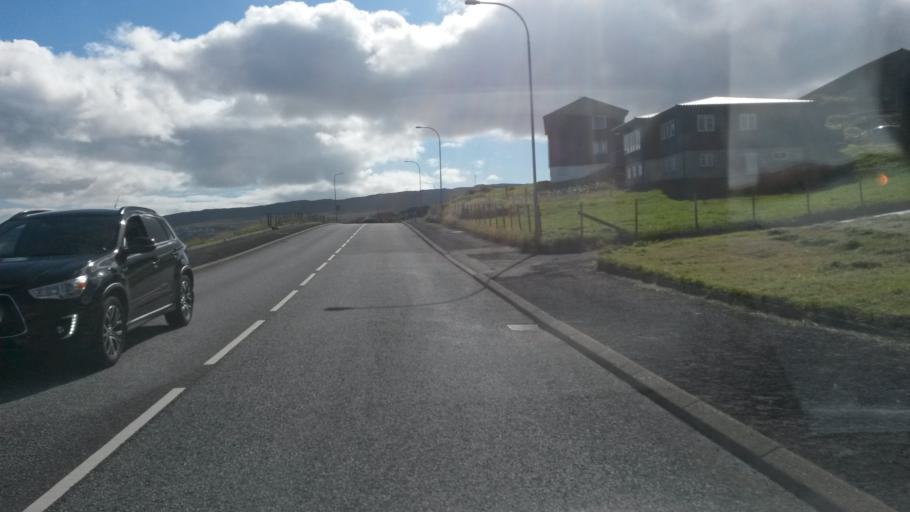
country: FO
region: Streymoy
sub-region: Torshavn
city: Torshavn
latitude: 62.0147
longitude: -6.7563
